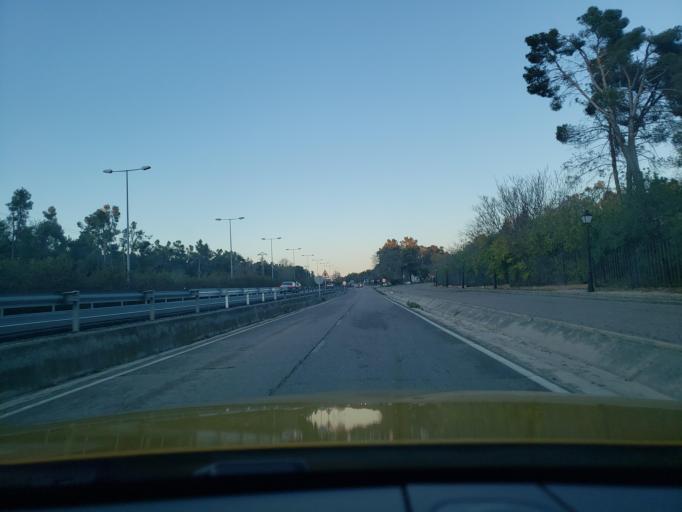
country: ES
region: Castille-La Mancha
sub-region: Province of Toledo
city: Bargas
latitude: 39.9197
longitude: -4.0053
